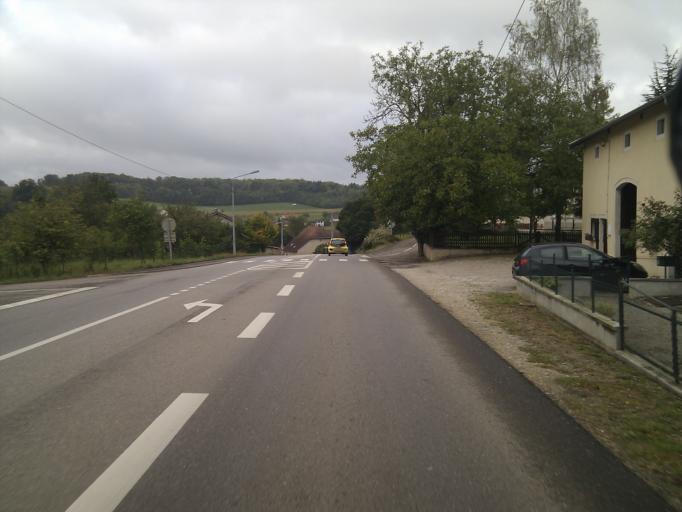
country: FR
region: Lorraine
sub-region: Departement des Vosges
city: Neufchateau
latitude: 48.4039
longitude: 5.7355
